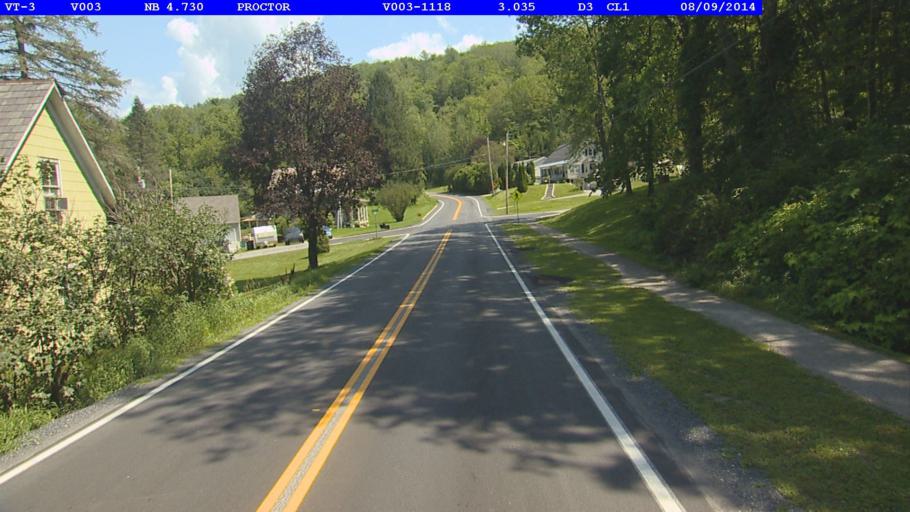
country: US
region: Vermont
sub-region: Rutland County
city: West Rutland
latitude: 43.6639
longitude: -73.0259
